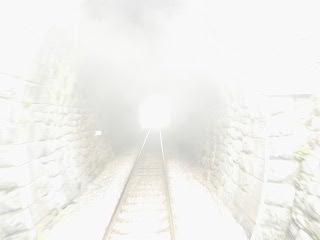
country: SI
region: Bled
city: Zasip
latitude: 46.4031
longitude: 14.0994
